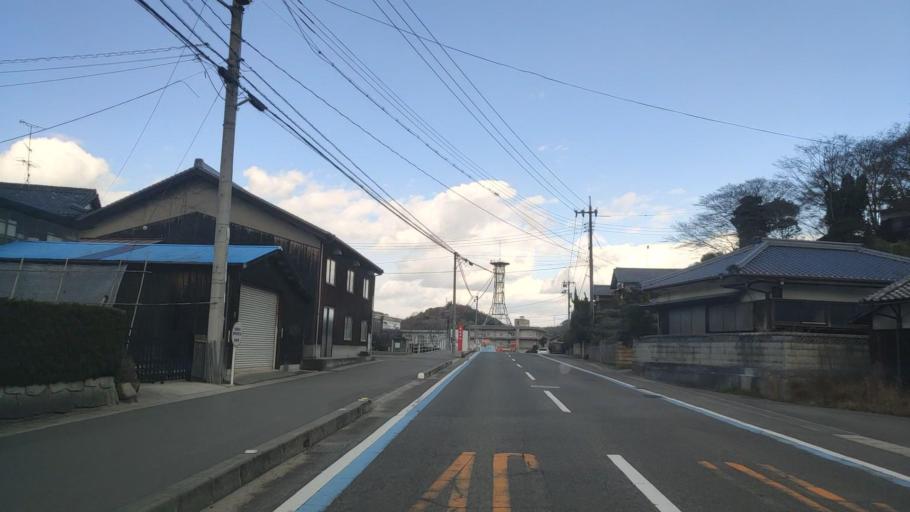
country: JP
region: Hiroshima
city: Innoshima
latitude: 34.2017
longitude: 133.1082
